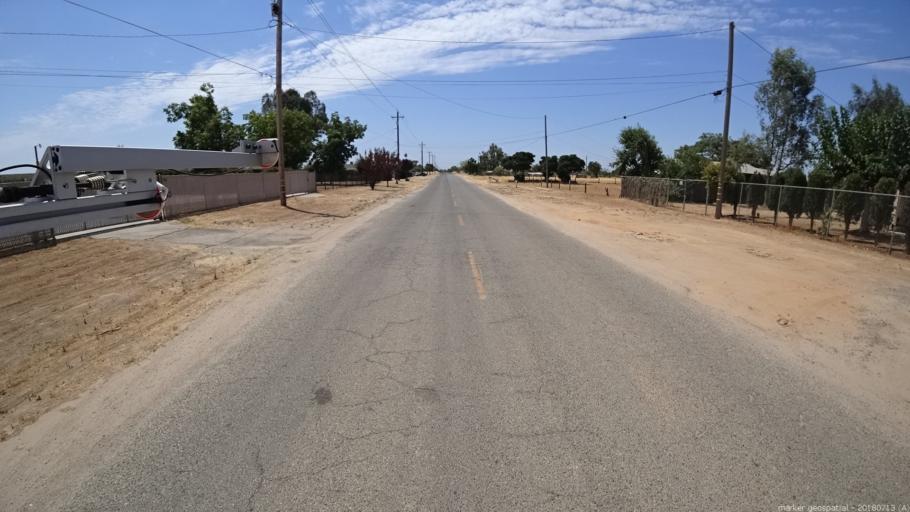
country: US
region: California
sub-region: Madera County
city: Madera
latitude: 36.9848
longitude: -120.0597
